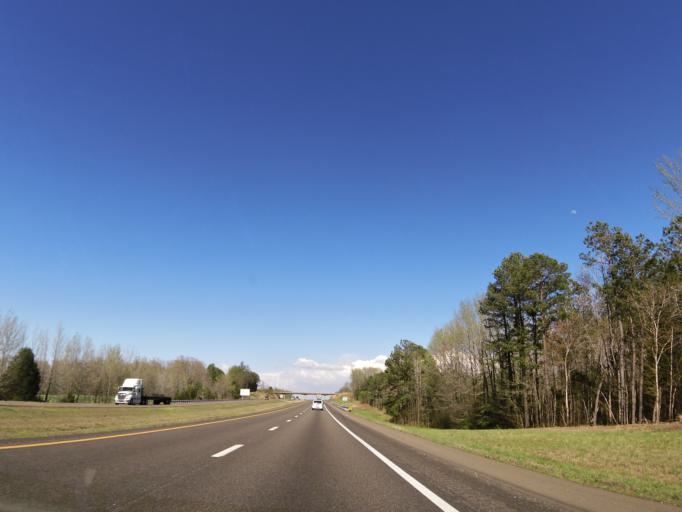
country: US
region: Tennessee
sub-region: Humphreys County
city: New Johnsonville
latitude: 35.8494
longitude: -88.0691
